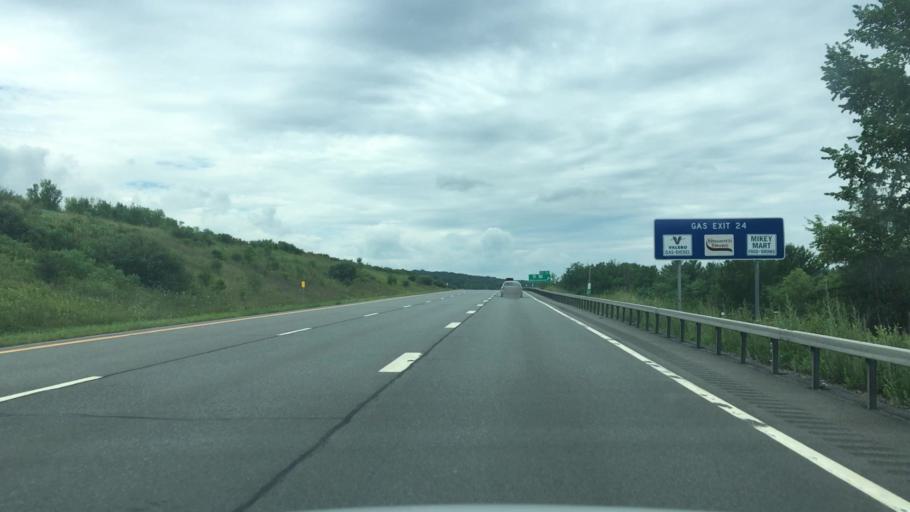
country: US
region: New York
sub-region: Albany County
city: Altamont
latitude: 42.7663
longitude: -74.1057
